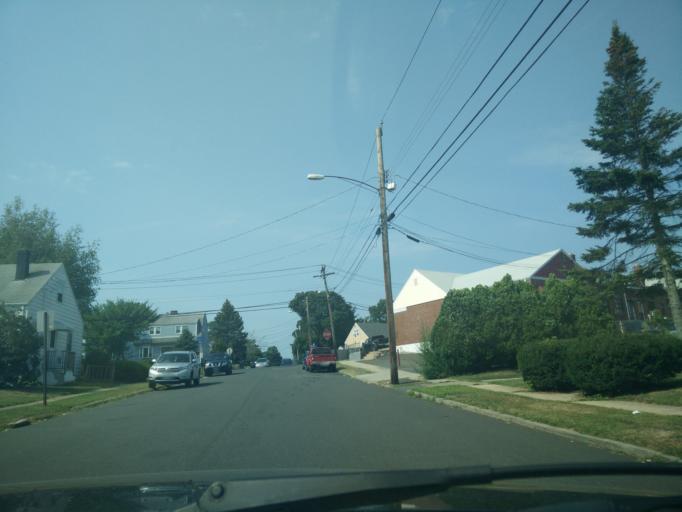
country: US
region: Connecticut
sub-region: Fairfield County
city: Bridgeport
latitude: 41.2057
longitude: -73.2207
